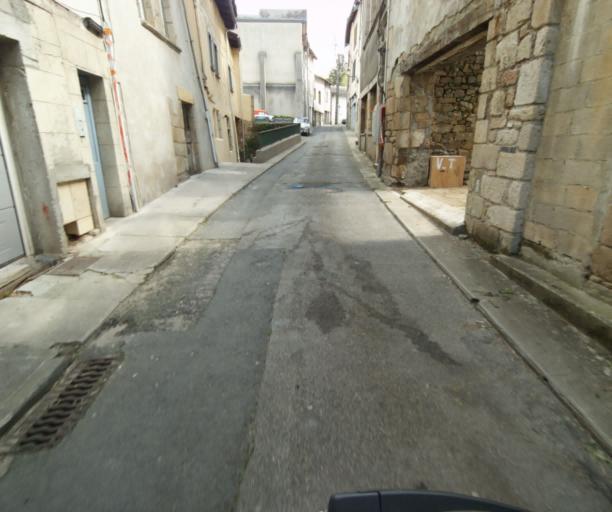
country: FR
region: Limousin
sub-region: Departement de la Correze
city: Tulle
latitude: 45.2692
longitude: 1.7745
